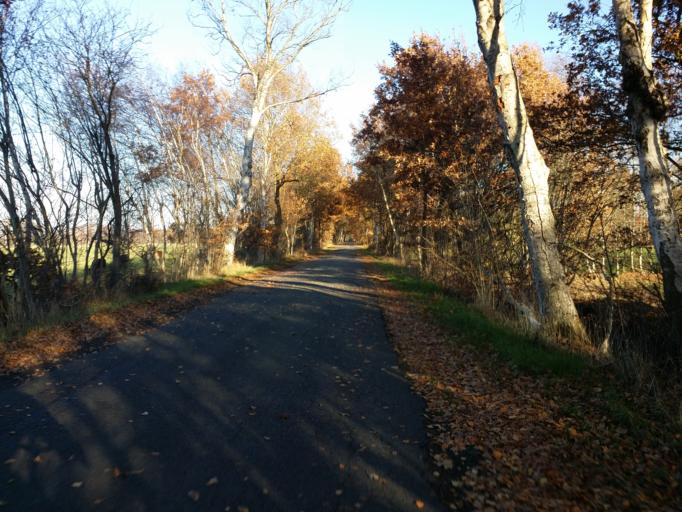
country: DE
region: Lower Saxony
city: Hellwege
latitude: 53.0324
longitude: 9.1933
